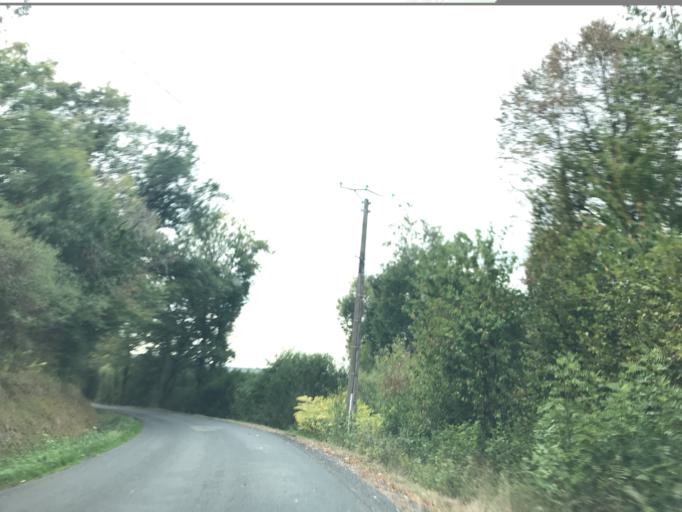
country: FR
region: Auvergne
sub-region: Departement du Puy-de-Dome
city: Courpiere
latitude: 45.7827
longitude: 3.5682
